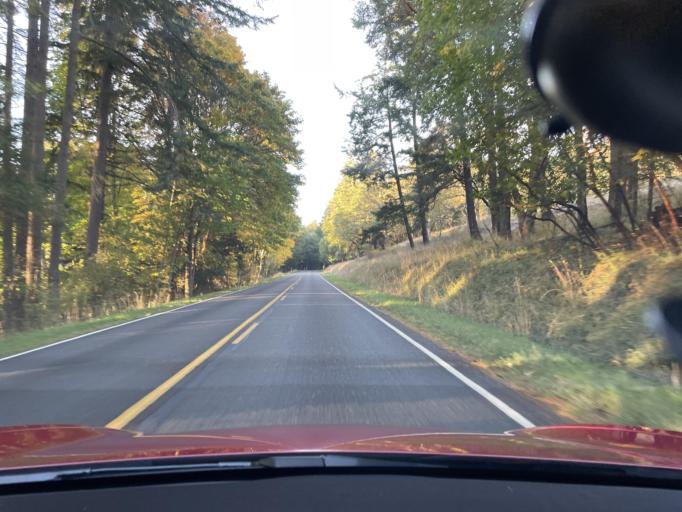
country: US
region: Washington
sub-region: San Juan County
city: Friday Harbor
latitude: 48.5808
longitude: -123.1439
